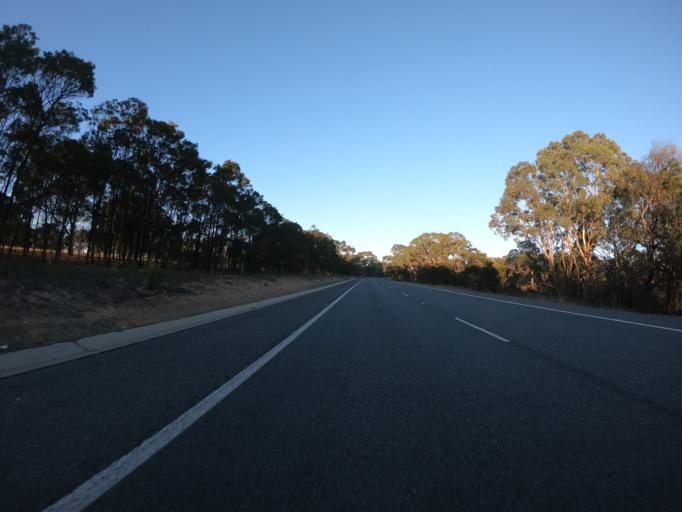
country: AU
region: New South Wales
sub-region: Goulburn Mulwaree
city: Goulburn
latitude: -34.8310
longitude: 149.5917
